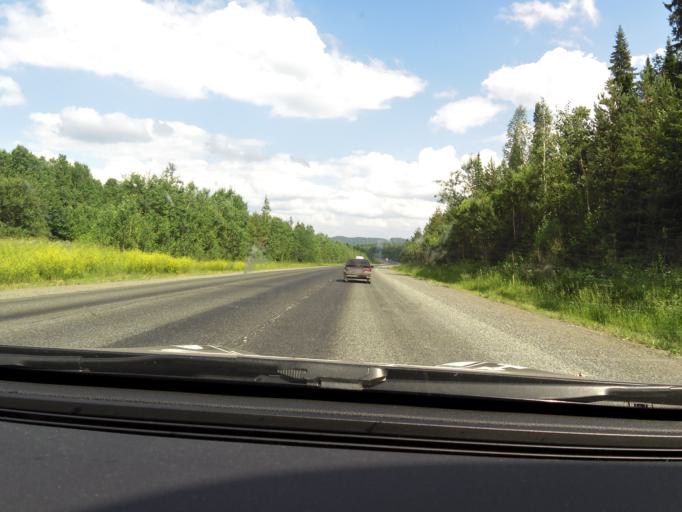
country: RU
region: Sverdlovsk
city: Arti
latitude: 56.7888
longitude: 58.5647
